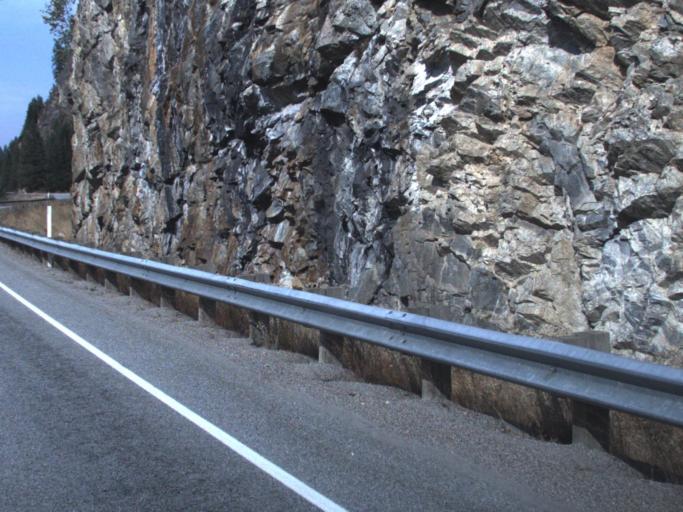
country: US
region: Washington
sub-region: Pend Oreille County
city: Newport
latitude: 48.2220
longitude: -117.2916
